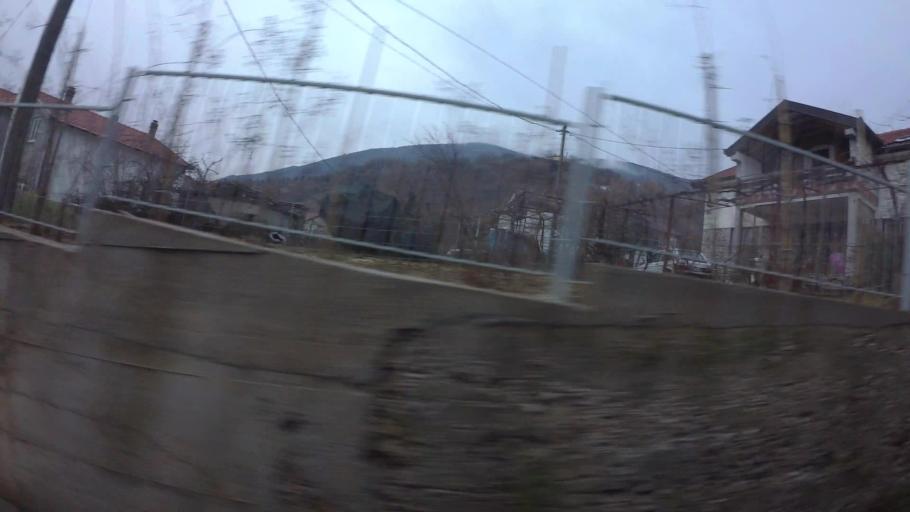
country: BA
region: Federation of Bosnia and Herzegovina
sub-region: Hercegovacko-Bosanski Kanton
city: Mostar
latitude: 43.3630
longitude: 17.8027
